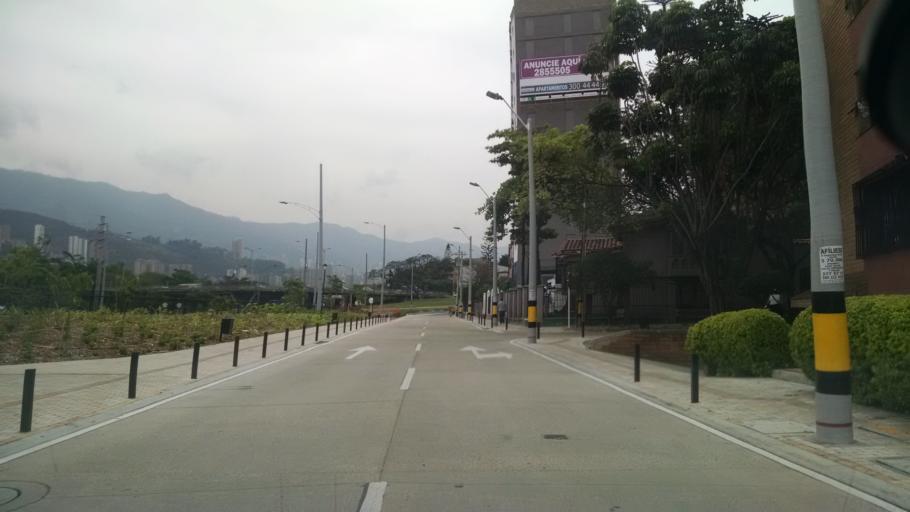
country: CO
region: Antioquia
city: Medellin
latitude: 6.2414
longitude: -75.5788
